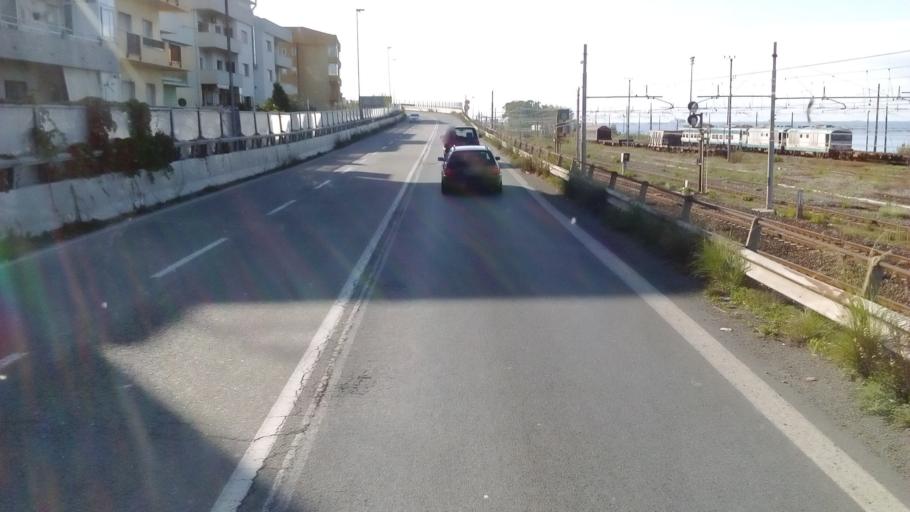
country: IT
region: Calabria
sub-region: Provincia di Reggio Calabria
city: Campo Calabro
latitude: 38.2090
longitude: 15.6355
